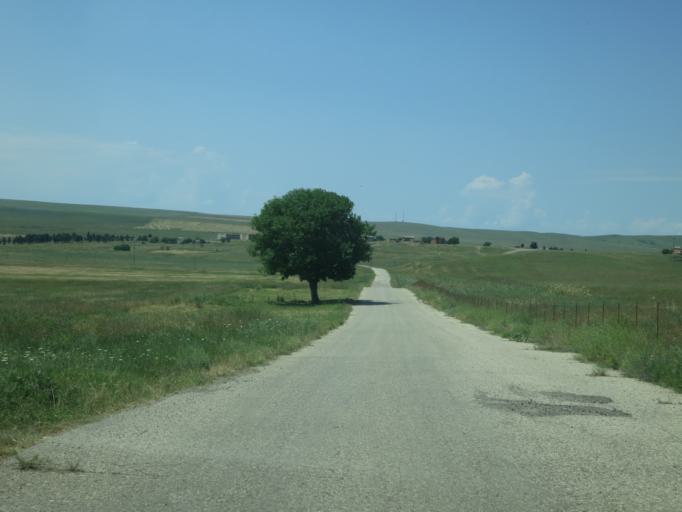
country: GE
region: Kakheti
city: Sagarejo
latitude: 41.5110
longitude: 45.3919
